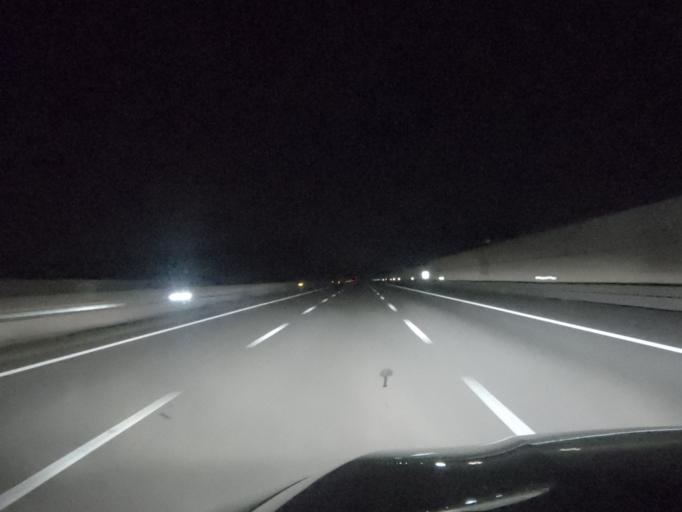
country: PT
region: Aveiro
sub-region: Estarreja
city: Avanca
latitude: 40.7979
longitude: -8.5492
